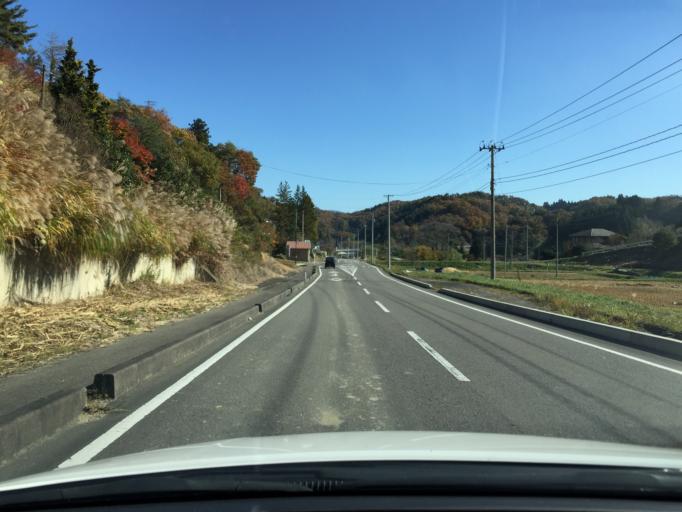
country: JP
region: Fukushima
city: Miharu
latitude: 37.4259
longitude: 140.5212
